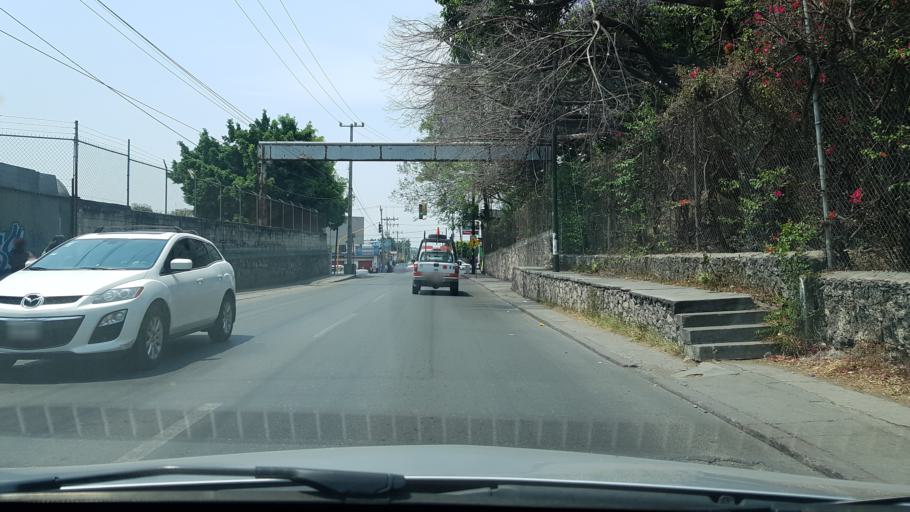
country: MX
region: Morelos
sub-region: Jiutepec
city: Jiutepec
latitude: 18.8912
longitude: -99.1726
